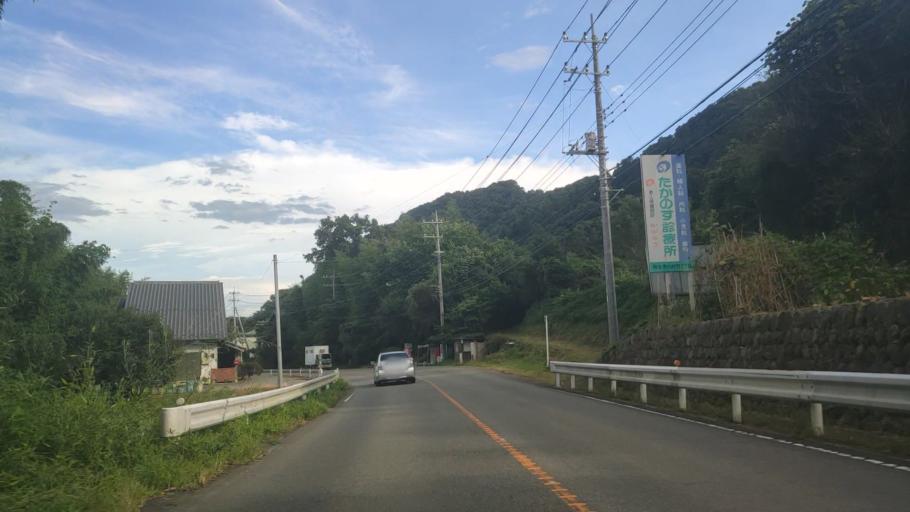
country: JP
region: Gunma
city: Omamacho-omama
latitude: 36.4620
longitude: 139.2596
